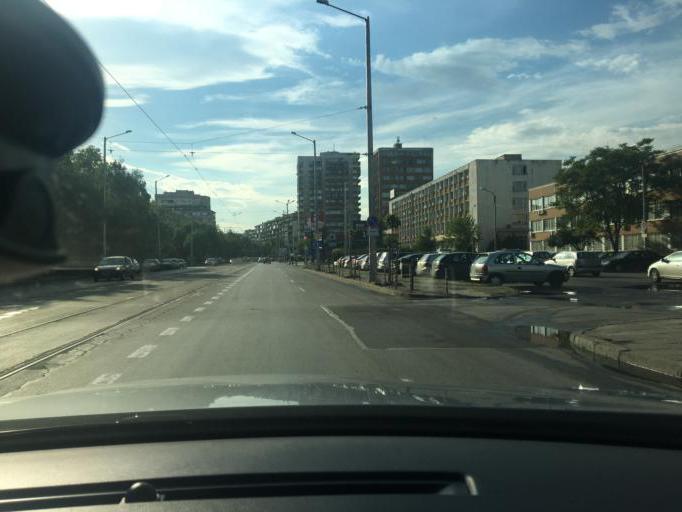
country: BG
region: Sofia-Capital
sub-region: Stolichna Obshtina
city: Sofia
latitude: 42.6773
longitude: 23.3685
